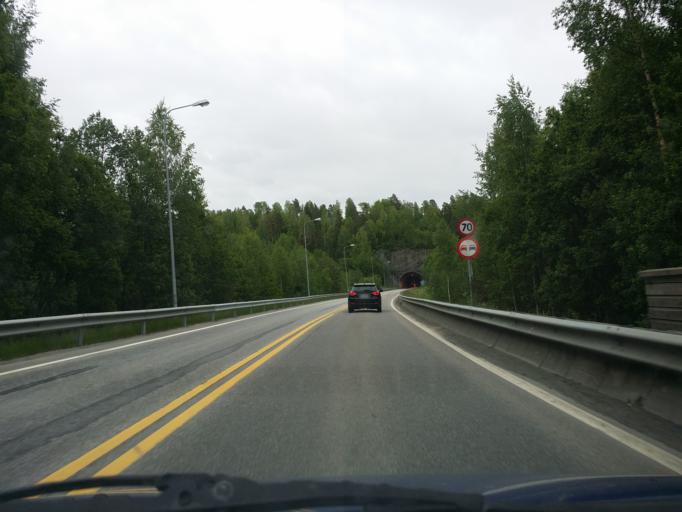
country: NO
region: Hedmark
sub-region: Ringsaker
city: Moelv
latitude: 60.9161
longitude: 10.7138
